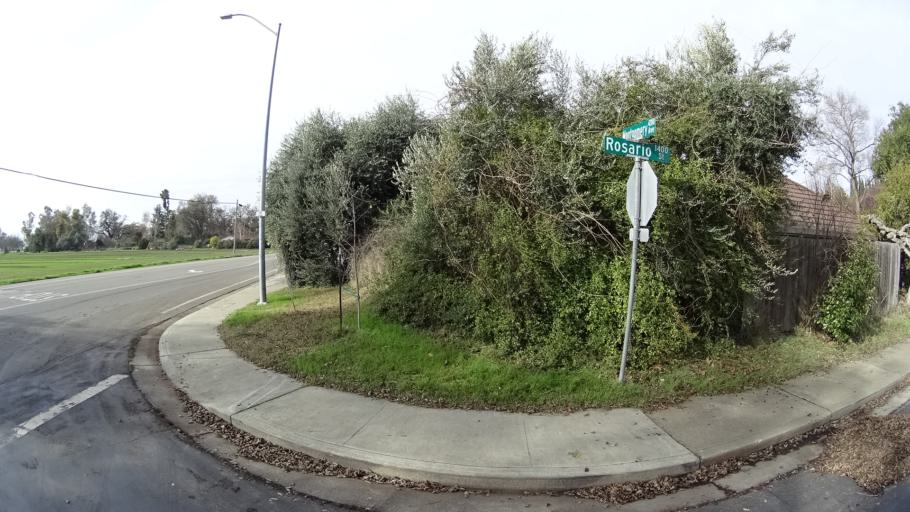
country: US
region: California
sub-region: Yolo County
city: Davis
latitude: 38.5388
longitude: -121.6992
